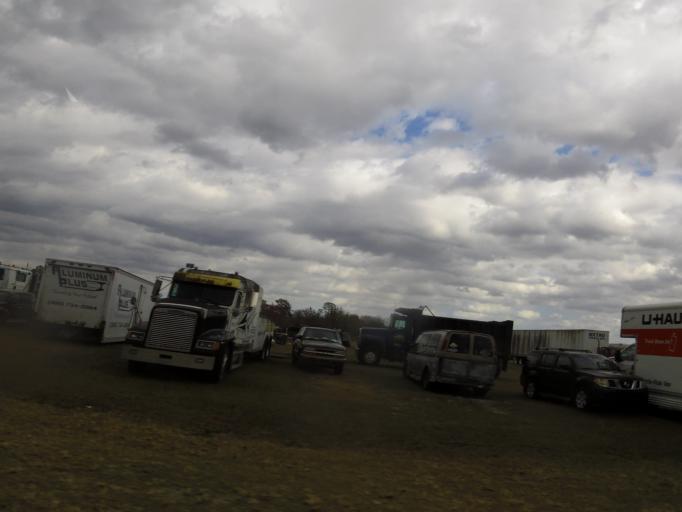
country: US
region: Florida
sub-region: Volusia County
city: Pierson
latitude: 29.3133
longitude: -81.4913
